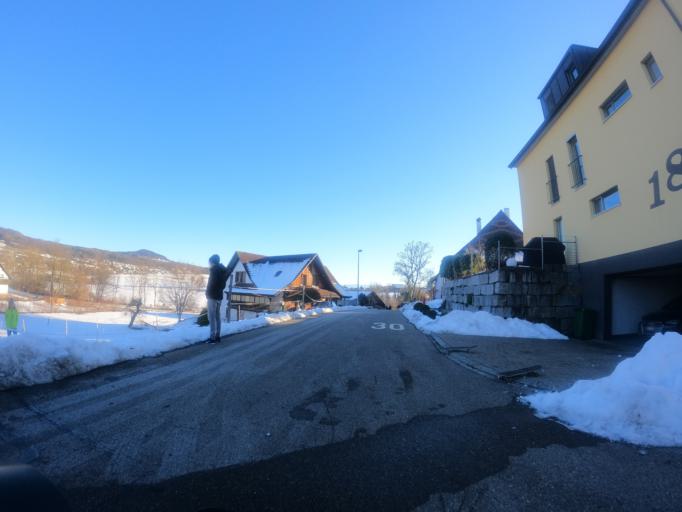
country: CH
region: Zurich
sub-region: Bezirk Affoltern
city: Affoltern / Unterdorf
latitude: 47.2883
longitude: 8.4391
